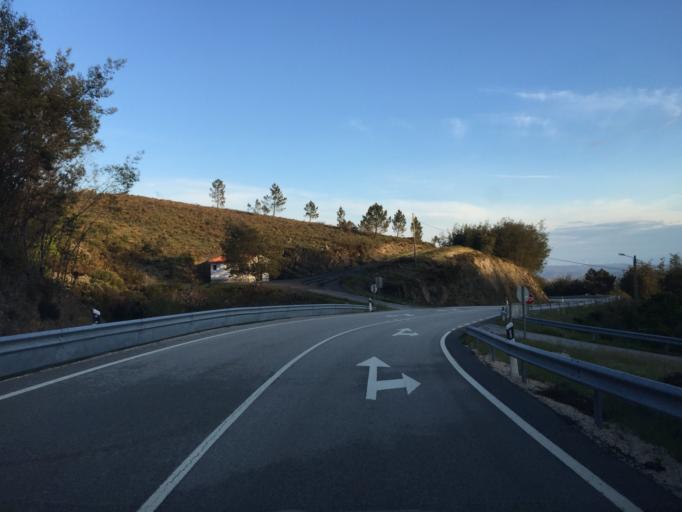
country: PT
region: Coimbra
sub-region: Pampilhosa da Serra
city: Pampilhosa da Serra
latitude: 40.1082
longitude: -8.0084
